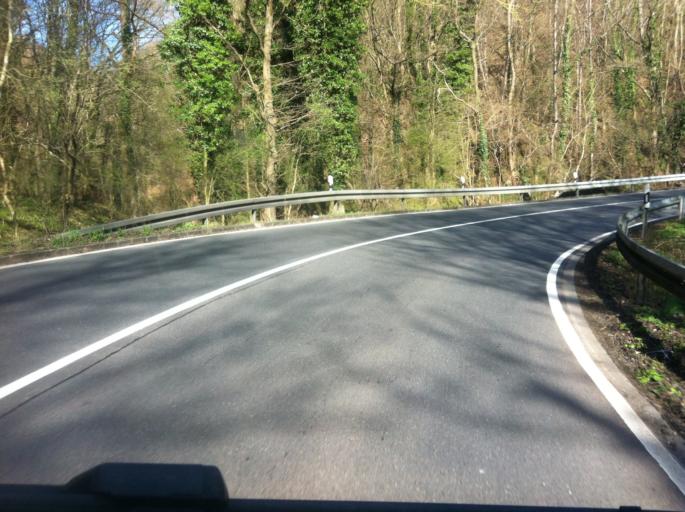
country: DE
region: North Rhine-Westphalia
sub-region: Regierungsbezirk Koln
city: Nideggen
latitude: 50.6922
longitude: 6.4762
